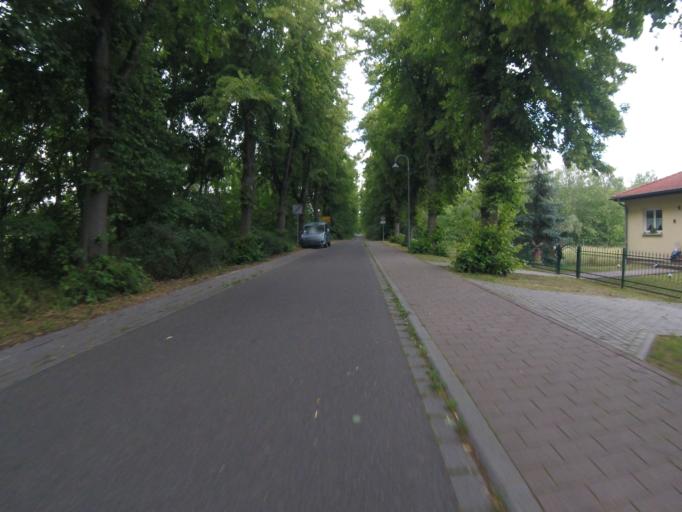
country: DE
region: Brandenburg
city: Konigs Wusterhausen
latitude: 52.3034
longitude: 13.5889
